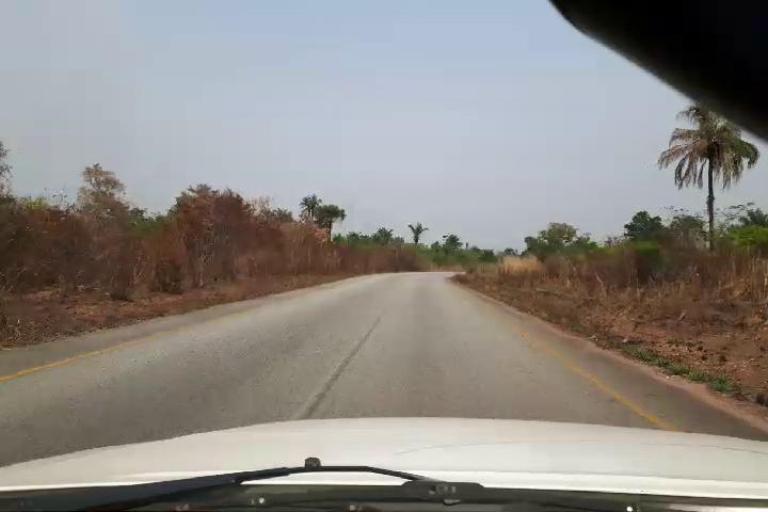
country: SL
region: Southern Province
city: Largo
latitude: 8.3003
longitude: -12.1997
